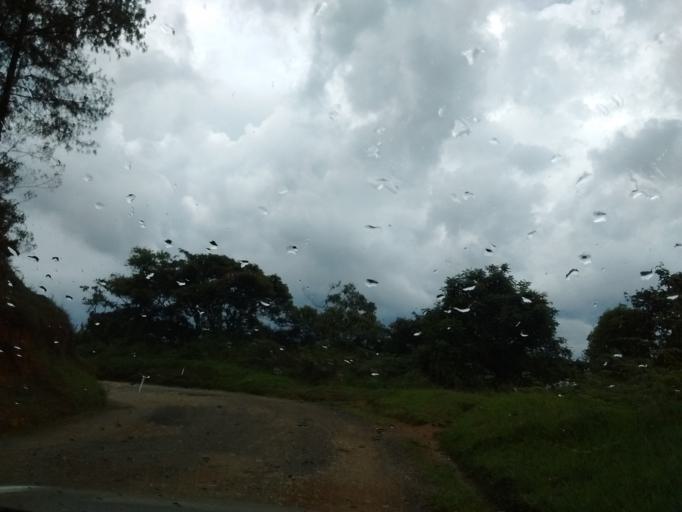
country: CO
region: Cauca
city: Cajibio
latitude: 2.5805
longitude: -76.6631
